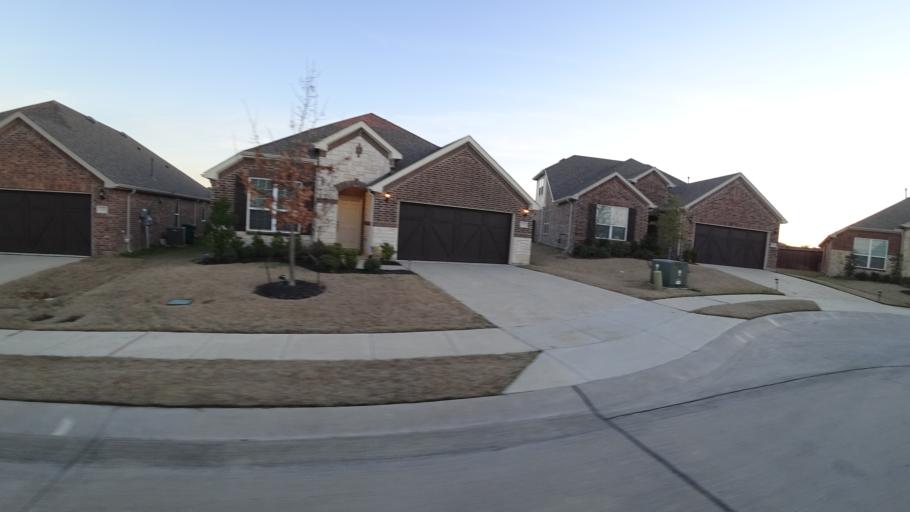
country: US
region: Texas
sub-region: Denton County
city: Lewisville
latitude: 32.9975
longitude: -96.9888
